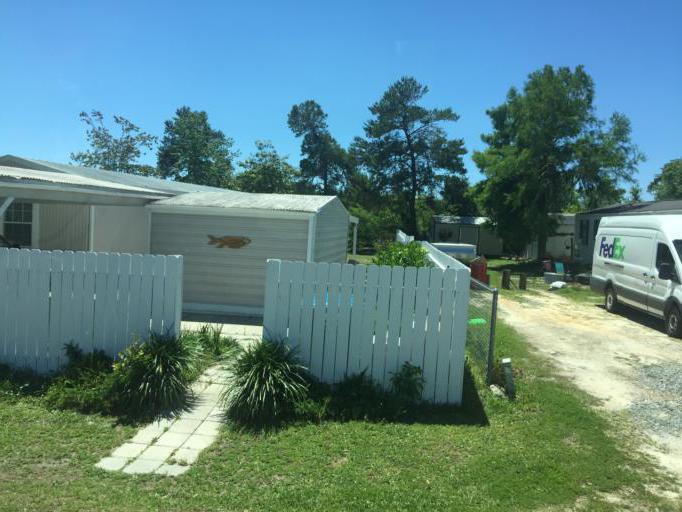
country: US
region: Florida
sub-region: Bay County
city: Laguna Beach
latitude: 30.2638
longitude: -85.9607
